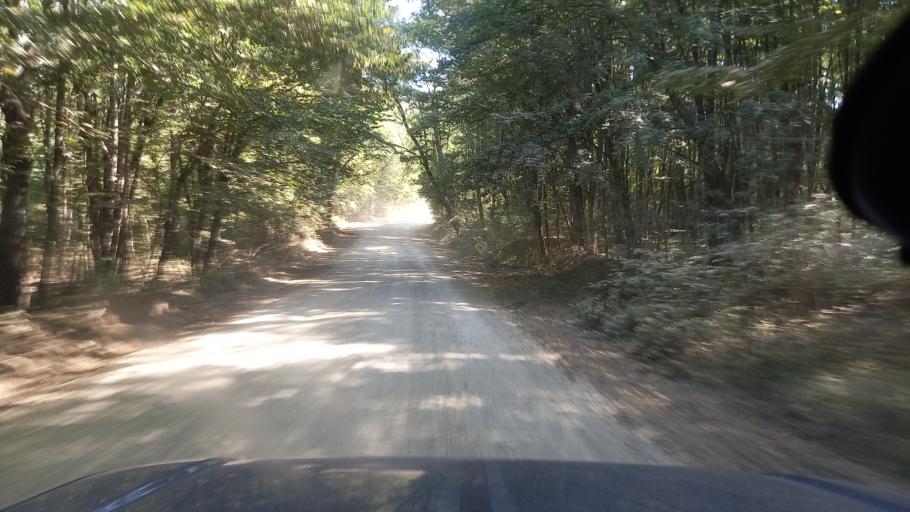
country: RU
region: Krasnodarskiy
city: Azovskaya
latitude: 44.6764
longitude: 38.6361
